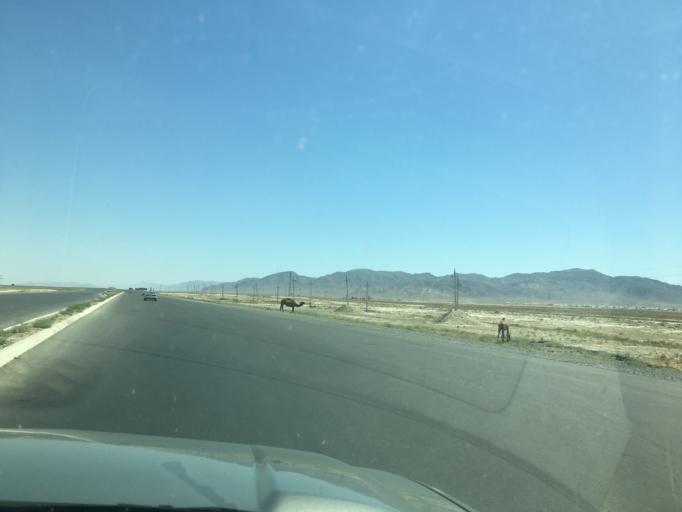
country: TM
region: Balkan
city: Serdar
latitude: 39.1092
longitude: 55.9266
